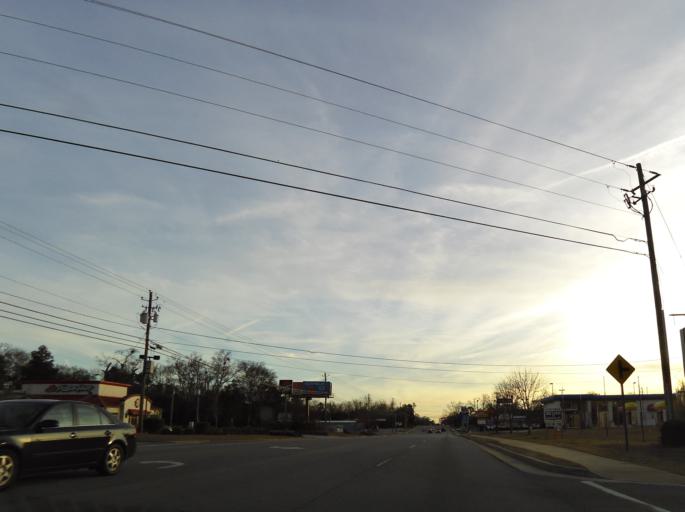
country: US
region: Georgia
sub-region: Bibb County
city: Macon
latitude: 32.7482
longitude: -83.6713
